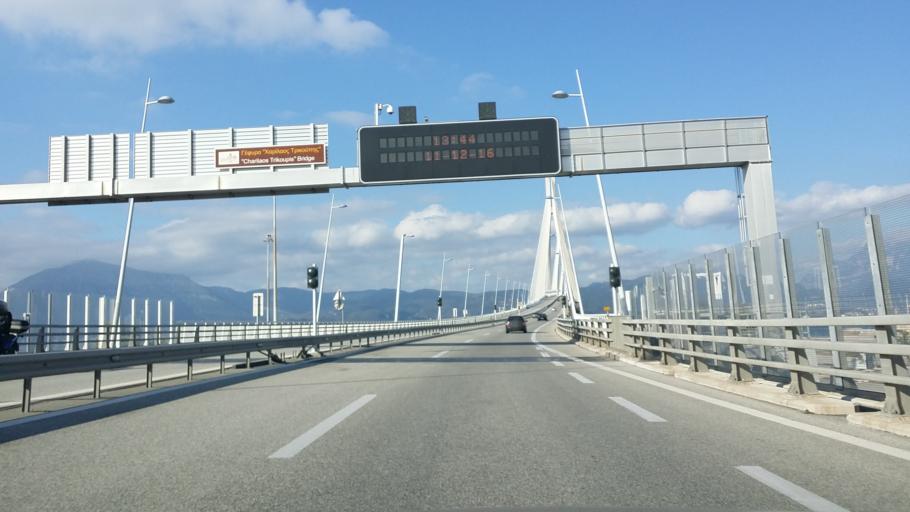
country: GR
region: West Greece
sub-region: Nomos Achaias
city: Rio
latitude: 38.3074
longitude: 21.7805
